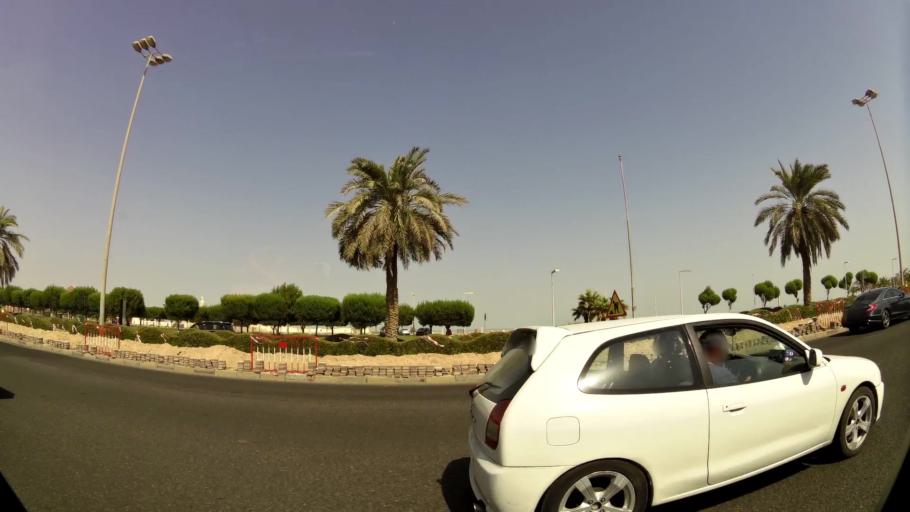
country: KW
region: Al Asimah
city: Ad Dasmah
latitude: 29.3682
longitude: 48.0143
